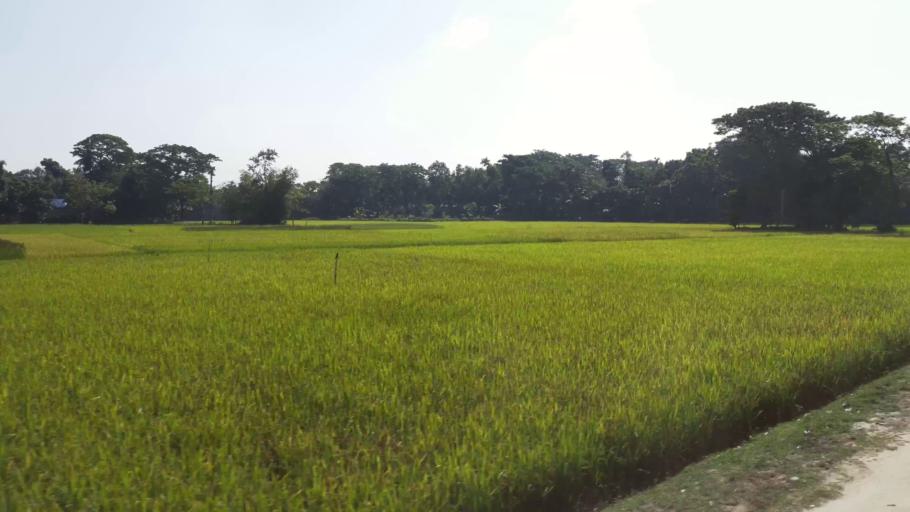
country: BD
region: Dhaka
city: Gafargaon
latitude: 24.4910
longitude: 90.5261
